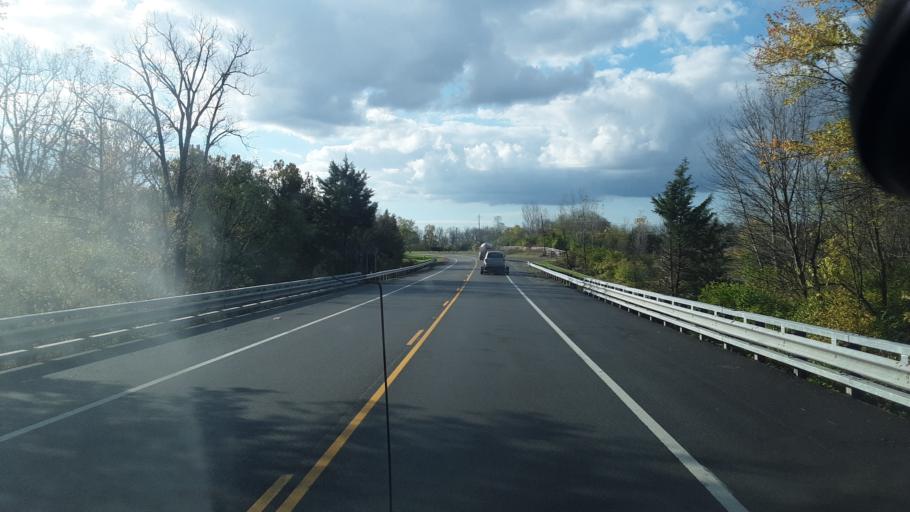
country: US
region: Ohio
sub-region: Fayette County
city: Washington Court House
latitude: 39.4694
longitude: -83.4345
